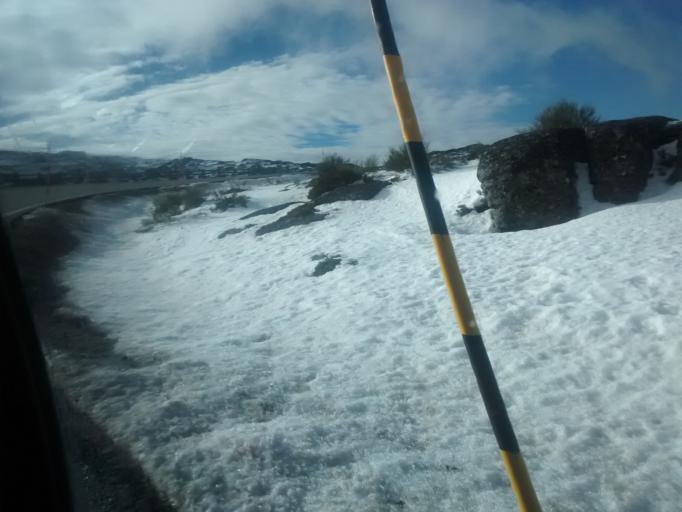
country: PT
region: Guarda
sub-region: Seia
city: Seia
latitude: 40.3499
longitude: -7.6620
